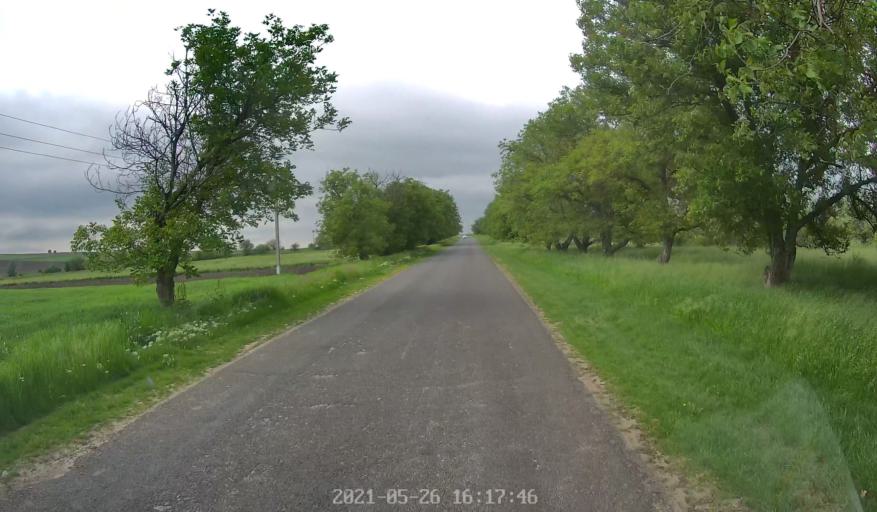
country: MD
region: Hincesti
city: Dancu
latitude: 46.7353
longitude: 28.3602
